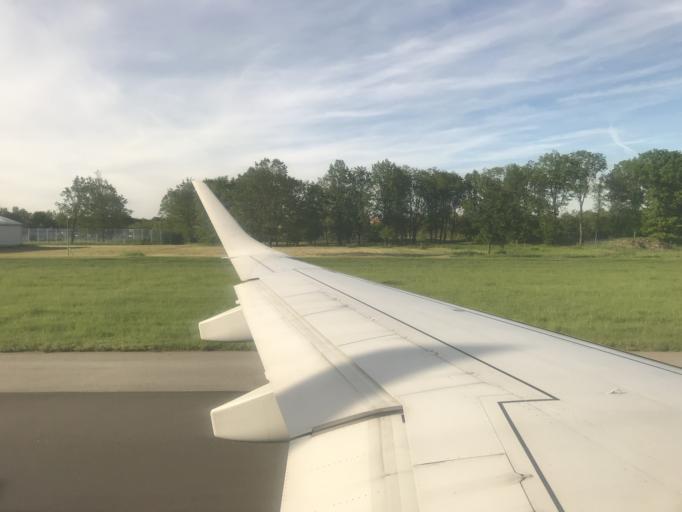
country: PL
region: Lower Silesian Voivodeship
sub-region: Powiat wroclawski
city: Smolec
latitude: 51.1056
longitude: 16.8879
